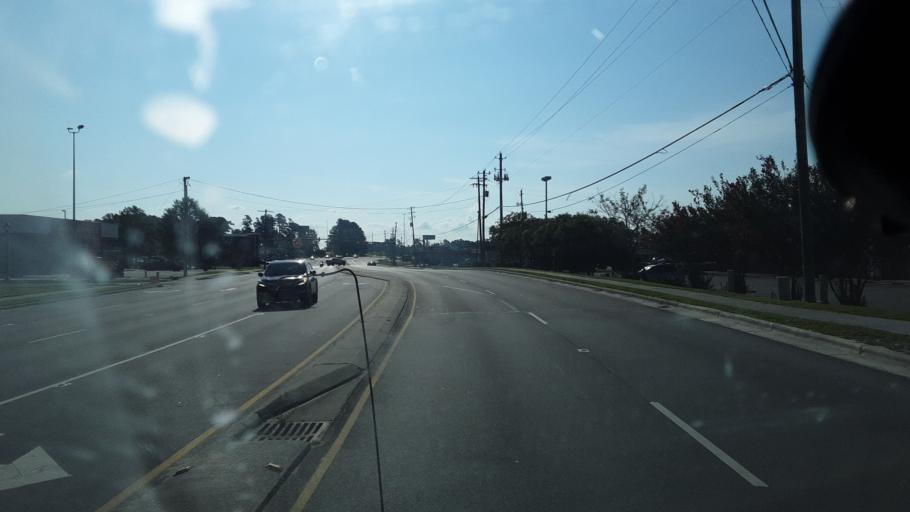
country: US
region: North Carolina
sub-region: Brunswick County
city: Navassa
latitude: 34.2343
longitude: -78.0004
